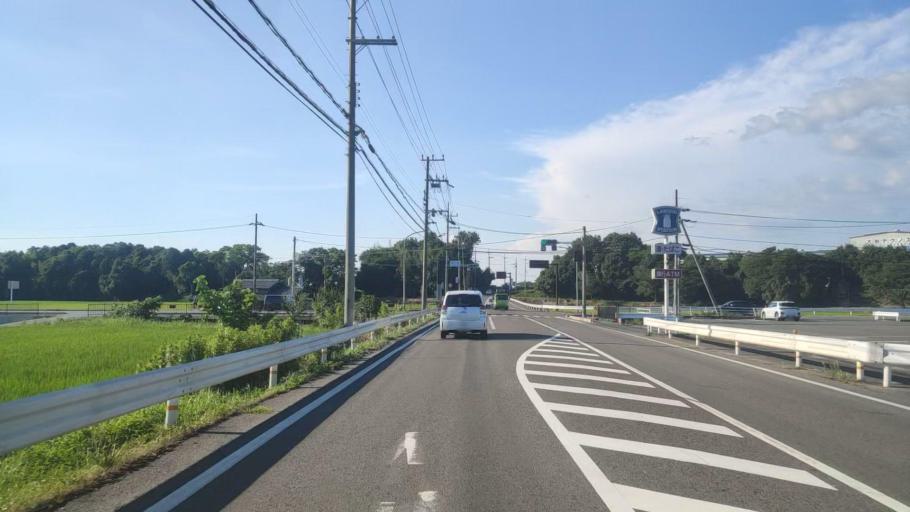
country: JP
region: Shiga Prefecture
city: Youkaichi
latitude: 35.1192
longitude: 136.2566
